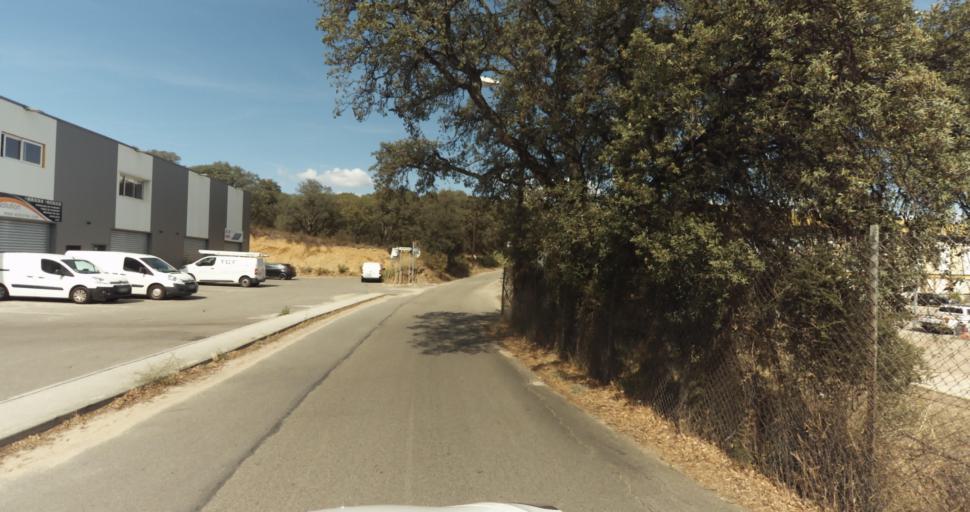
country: FR
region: Corsica
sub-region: Departement de la Corse-du-Sud
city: Alata
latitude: 41.9501
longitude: 8.7661
